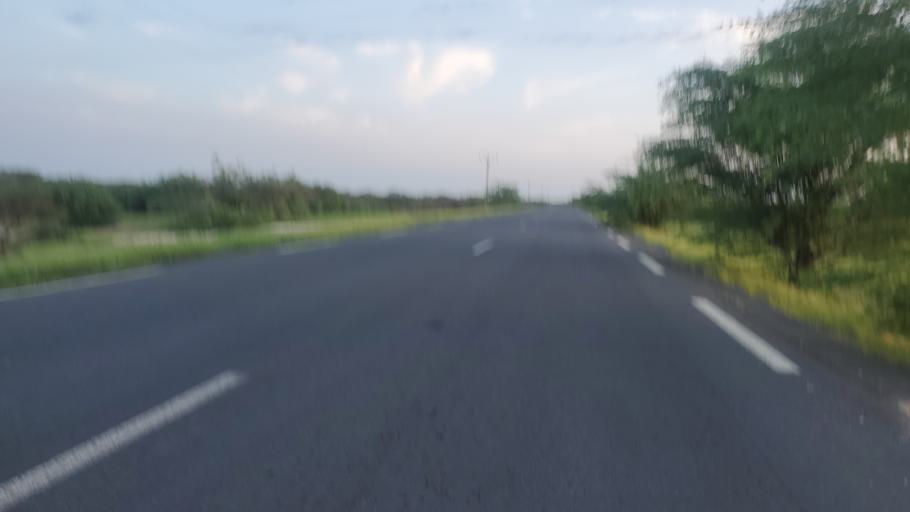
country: SN
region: Saint-Louis
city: Saint-Louis
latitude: 16.1272
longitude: -16.4132
